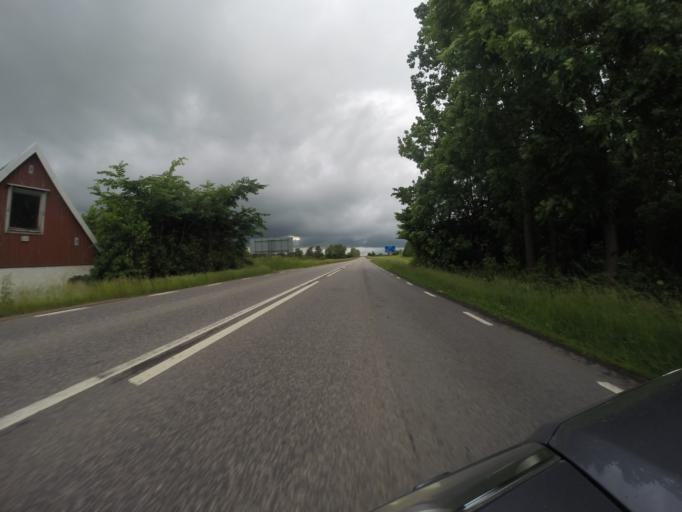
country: SE
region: Skane
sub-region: Landskrona
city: Asmundtorp
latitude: 55.8927
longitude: 12.9637
